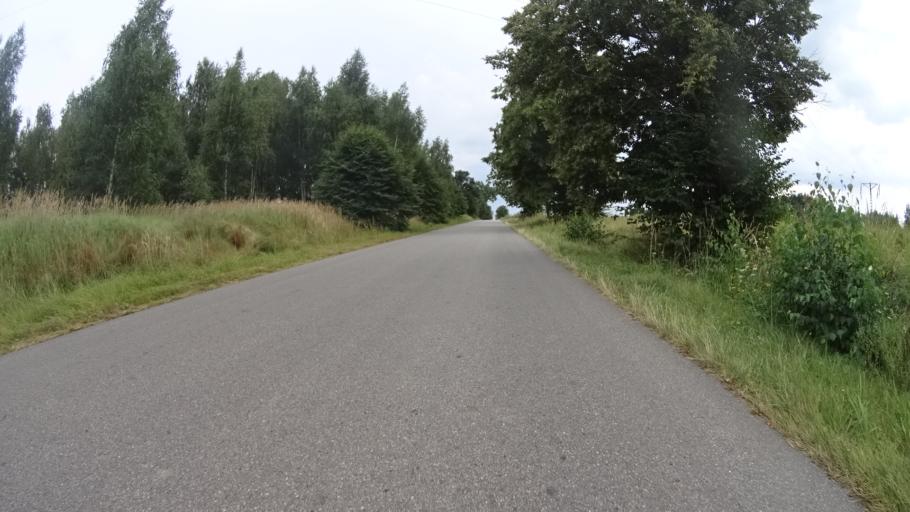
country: PL
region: Masovian Voivodeship
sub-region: Powiat grojecki
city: Goszczyn
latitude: 51.6701
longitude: 20.8569
